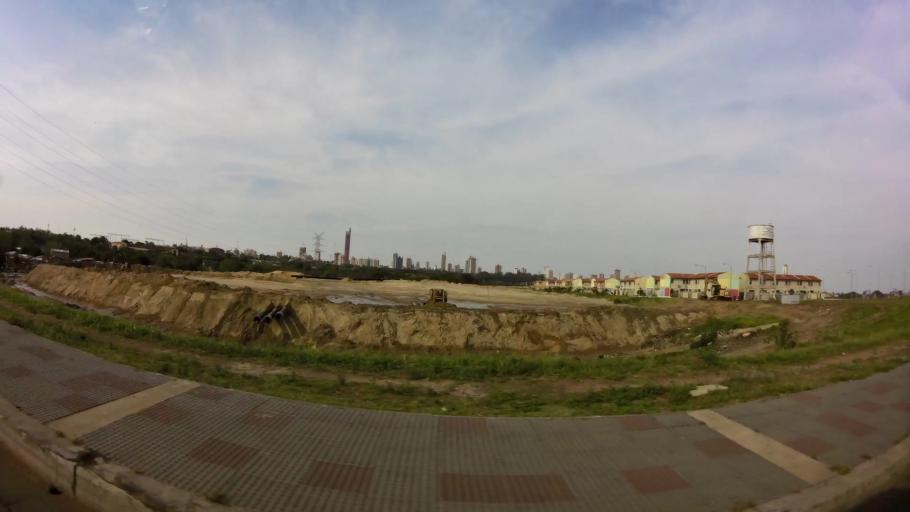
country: PY
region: Asuncion
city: Asuncion
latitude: -25.2711
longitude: -57.6124
